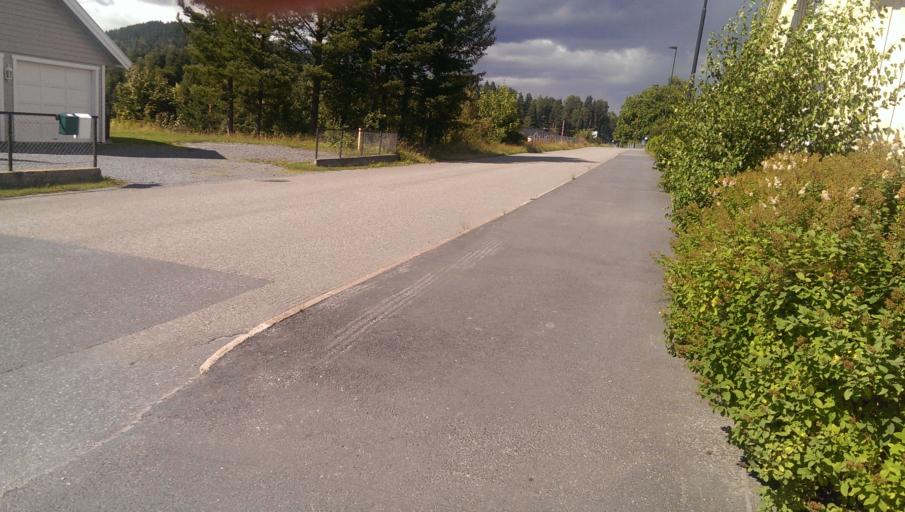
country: NO
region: Buskerud
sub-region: Kongsberg
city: Kongsberg
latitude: 59.6563
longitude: 9.6534
